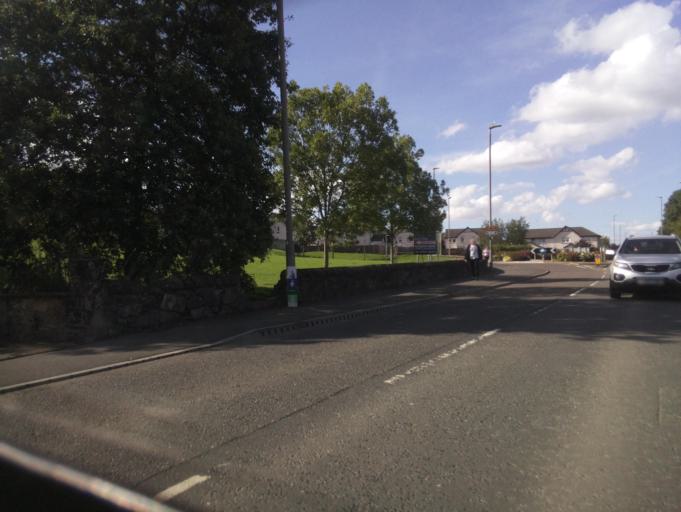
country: GB
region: Scotland
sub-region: Stirling
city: Plean
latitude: 56.0627
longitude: -3.8726
